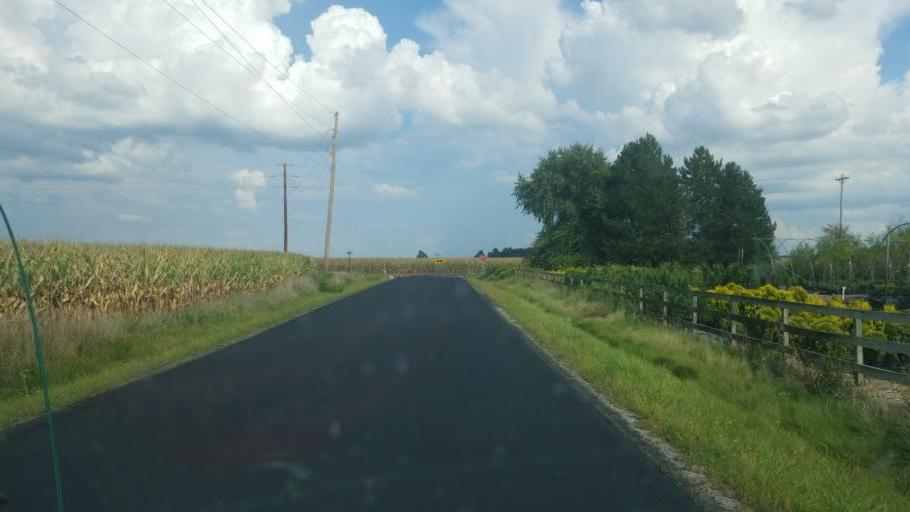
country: US
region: Ohio
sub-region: Huron County
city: Willard
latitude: 40.9936
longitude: -82.8543
